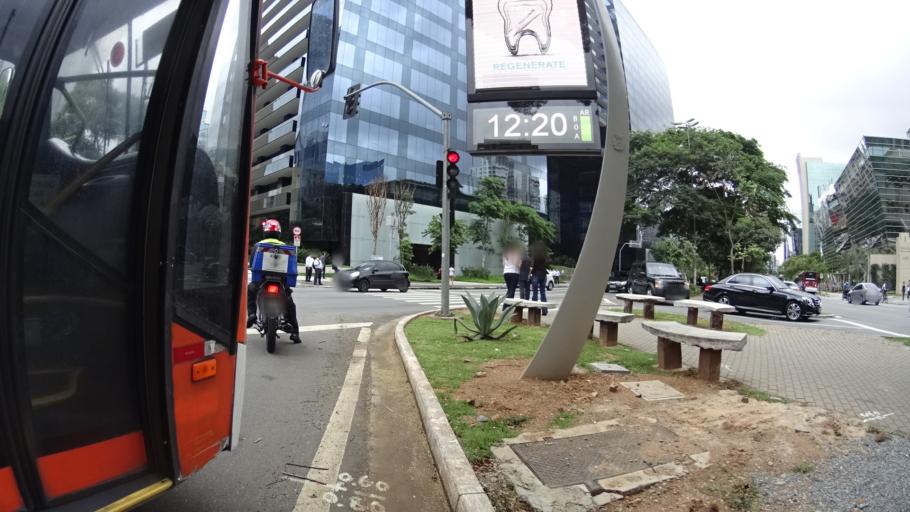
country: BR
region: Sao Paulo
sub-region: Sao Paulo
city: Sao Paulo
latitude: -23.5857
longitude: -46.6829
